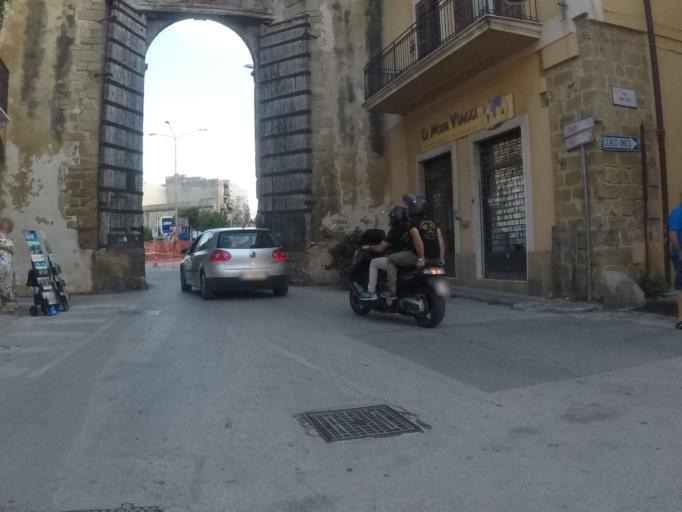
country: IT
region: Sicily
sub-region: Agrigento
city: Sciacca
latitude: 37.5105
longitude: 13.0794
